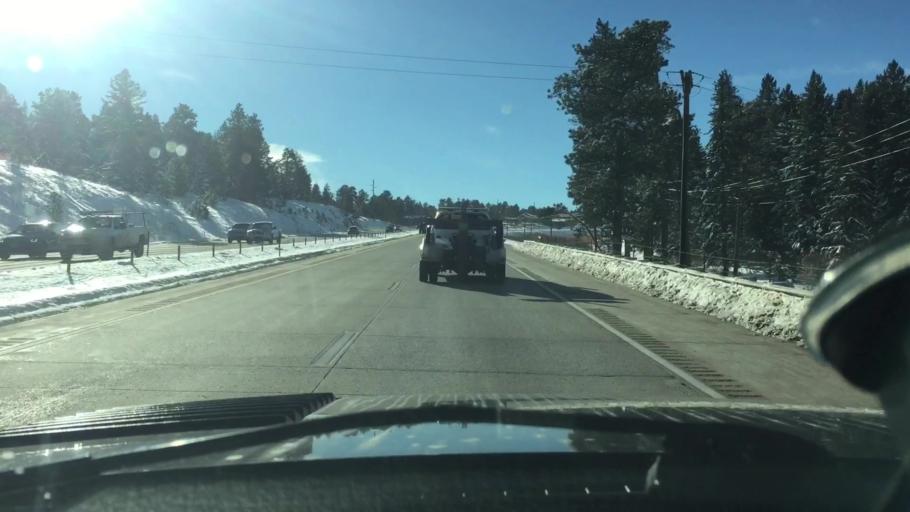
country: US
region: Colorado
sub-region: Jefferson County
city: Indian Hills
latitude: 39.5712
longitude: -105.2397
